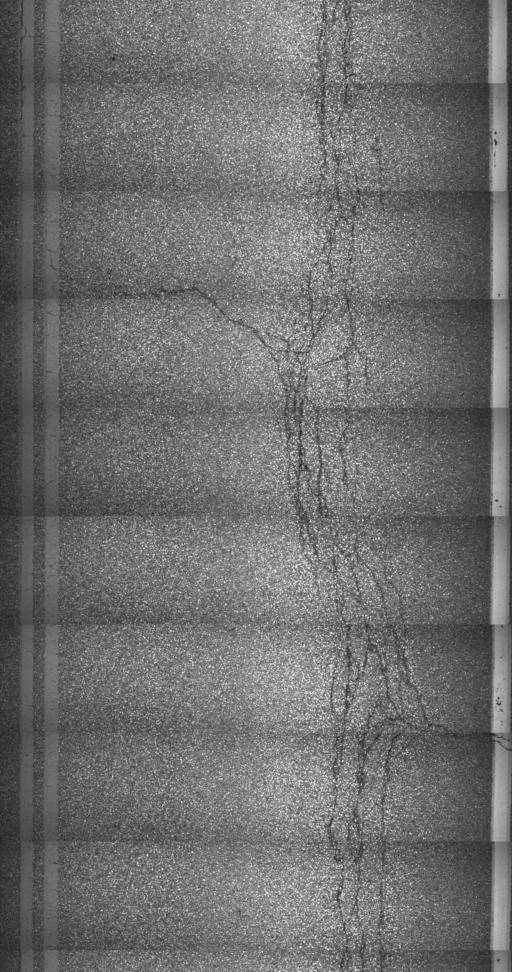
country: US
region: Vermont
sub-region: Rutland County
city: Rutland
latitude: 43.5364
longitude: -72.7434
